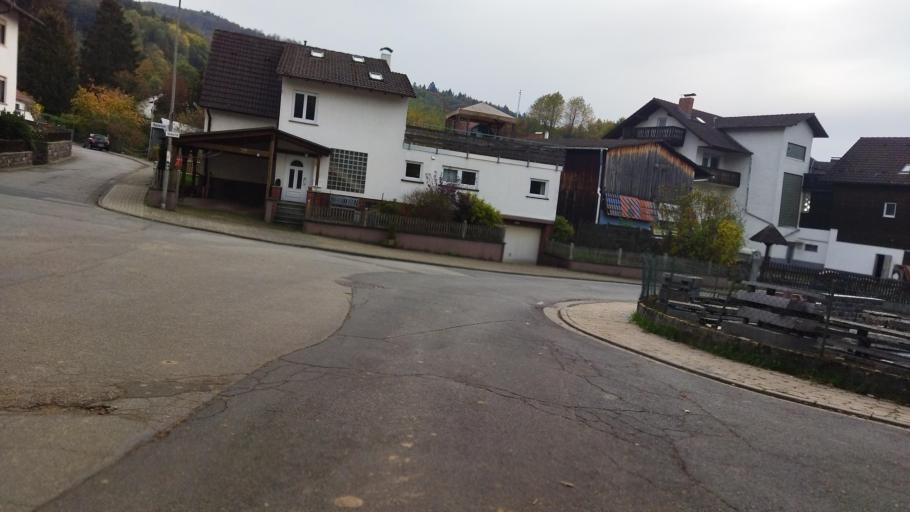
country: DE
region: Hesse
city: Lutzelbach
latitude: 49.7097
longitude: 8.7034
